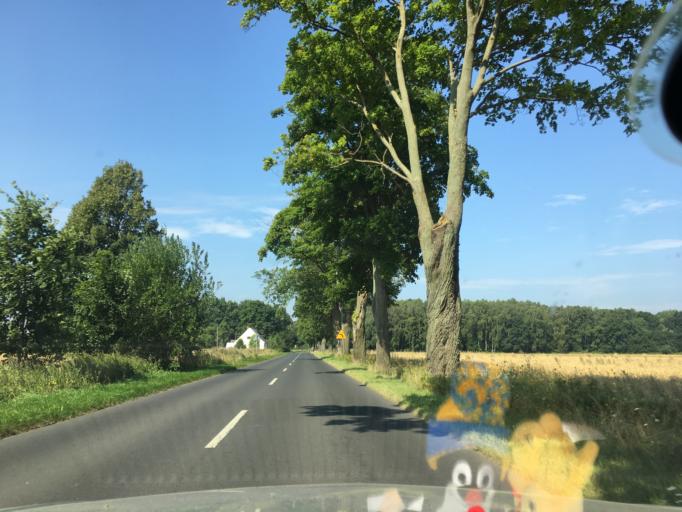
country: PL
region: West Pomeranian Voivodeship
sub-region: Powiat gryficki
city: Pobierowo
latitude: 54.0134
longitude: 14.8606
